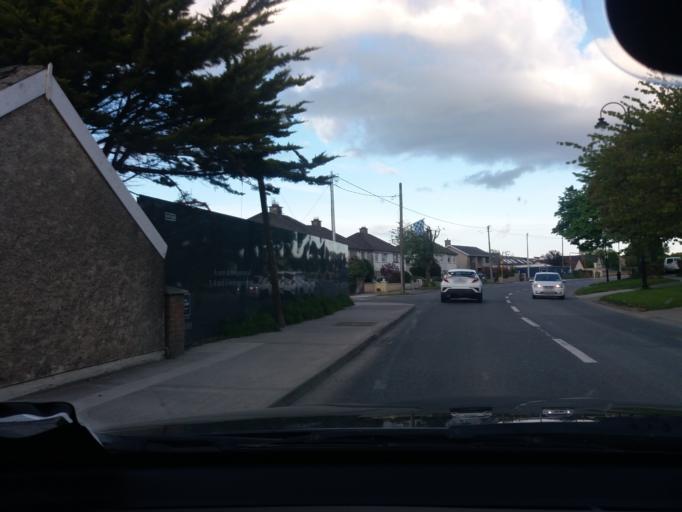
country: IE
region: Leinster
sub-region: South Dublin
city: Newcastle
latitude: 53.2997
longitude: -6.4978
